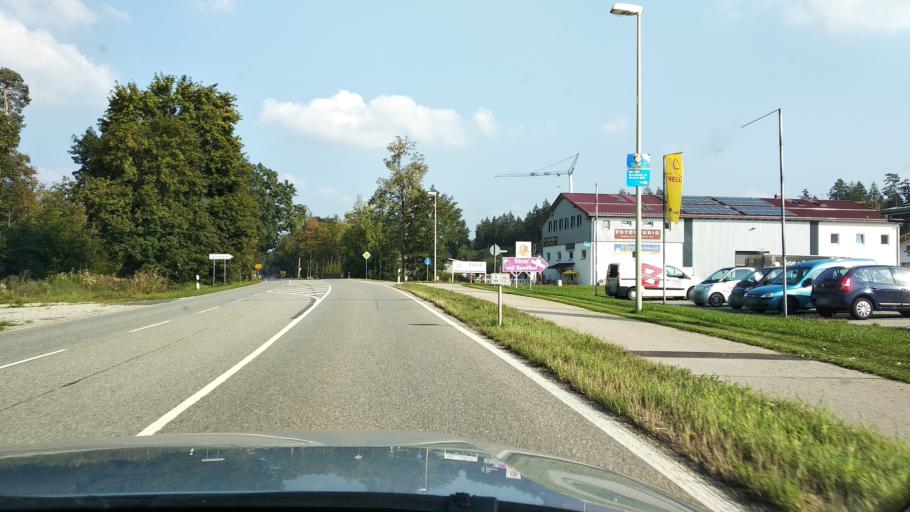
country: DE
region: Bavaria
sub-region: Upper Bavaria
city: Pfaffing
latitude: 48.0799
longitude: 12.0961
